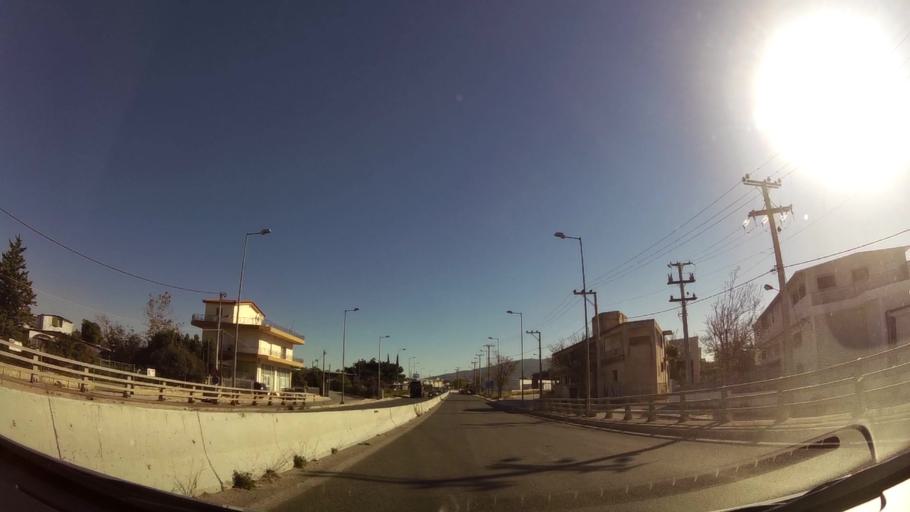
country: GR
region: Attica
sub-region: Nomarchia Athinas
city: Metamorfosi
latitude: 38.0925
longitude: 23.7718
